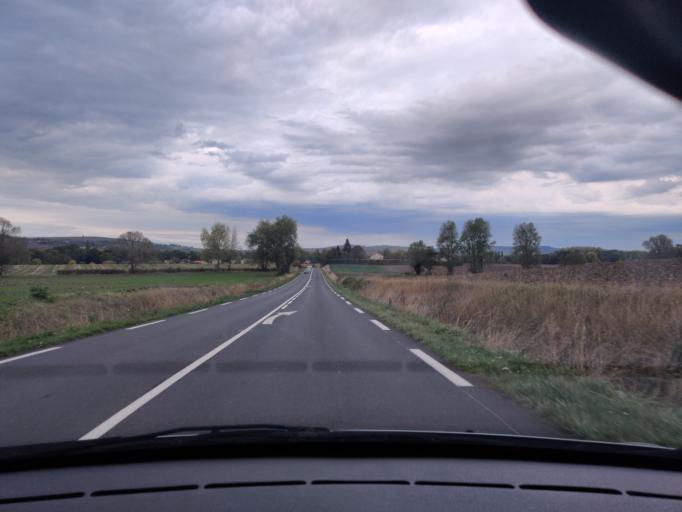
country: FR
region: Auvergne
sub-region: Departement du Puy-de-Dome
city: Saint-Bonnet-pres-Riom
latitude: 45.9380
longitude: 3.1114
